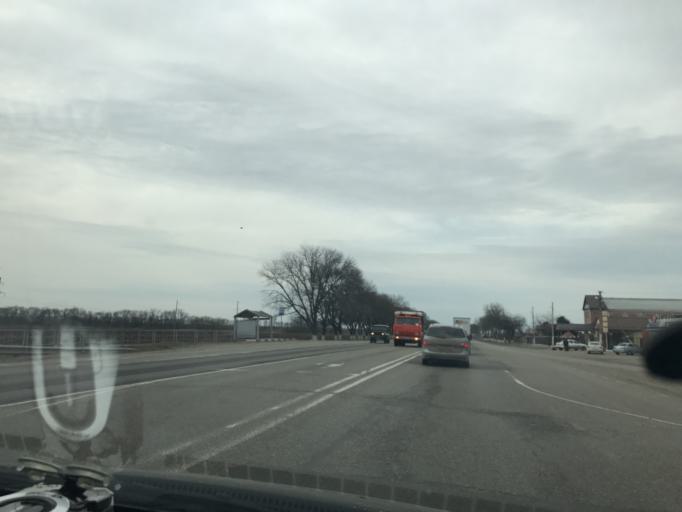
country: RU
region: Krasnodarskiy
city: Zavetnyy
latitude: 44.9241
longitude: 41.1306
